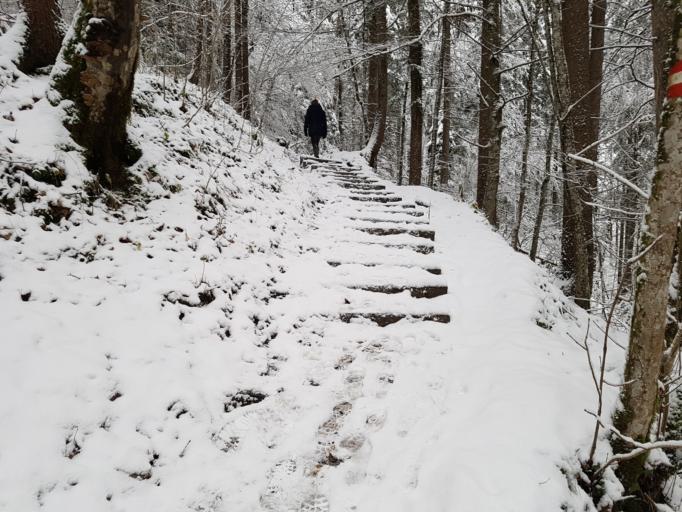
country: DE
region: Bavaria
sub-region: Upper Bavaria
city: Piding
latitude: 47.7349
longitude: 12.9466
